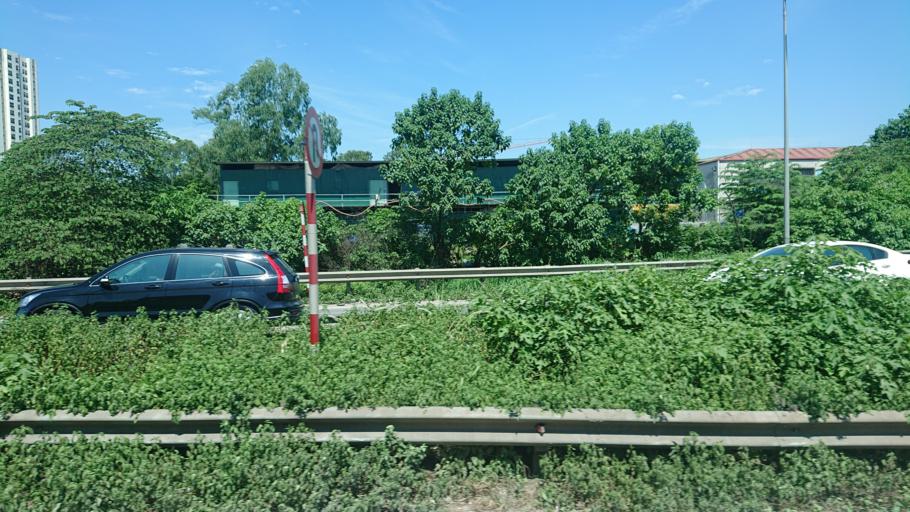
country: VN
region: Ha Noi
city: Van Dien
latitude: 20.9643
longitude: 105.8472
